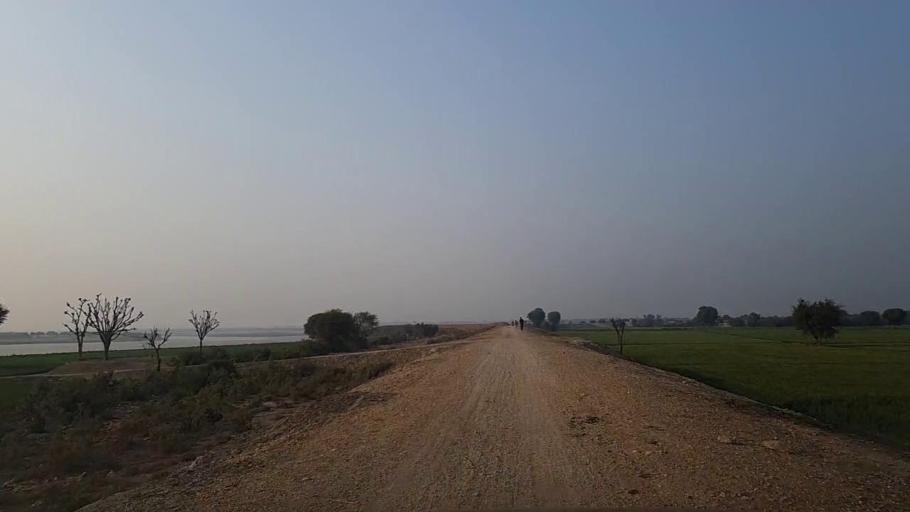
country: PK
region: Sindh
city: Sann
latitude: 26.1301
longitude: 68.1396
